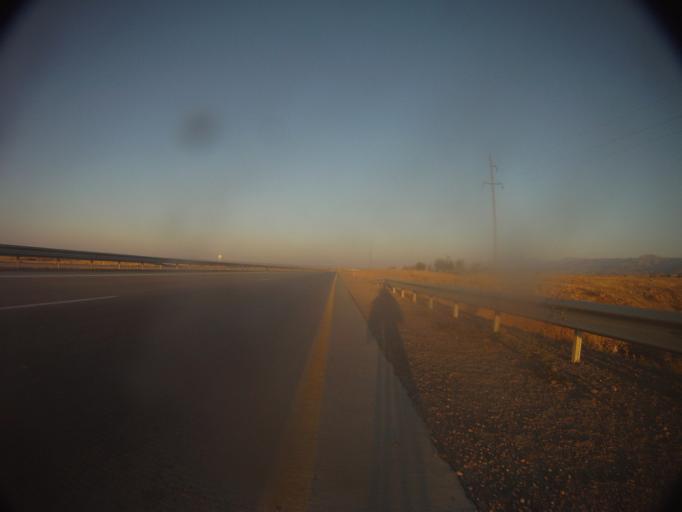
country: KZ
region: Zhambyl
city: Sarykemer
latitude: 43.0106
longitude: 71.6616
